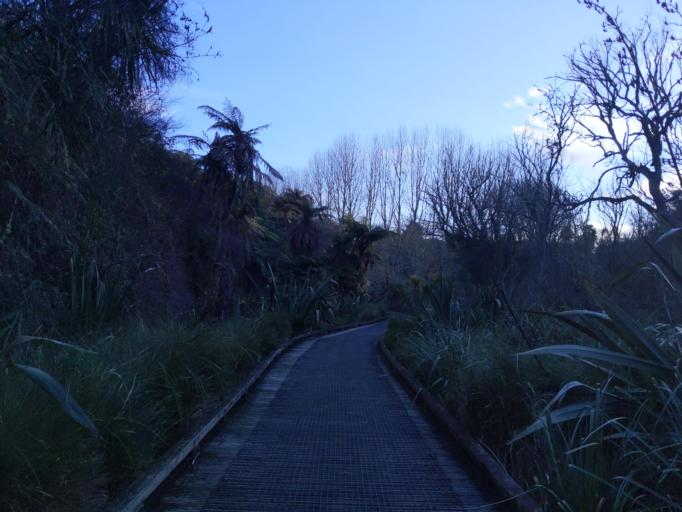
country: NZ
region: Waikato
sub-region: Hamilton City
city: Hamilton
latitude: -37.7386
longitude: 175.2769
